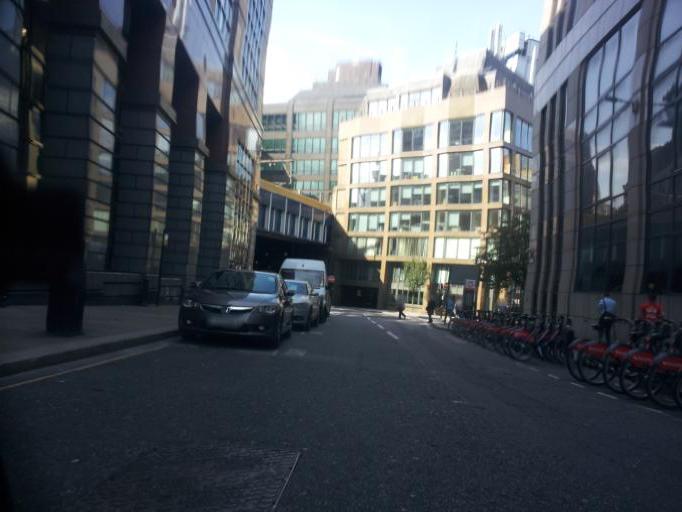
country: GB
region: England
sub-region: Greater London
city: City of London
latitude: 51.5115
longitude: -0.0767
